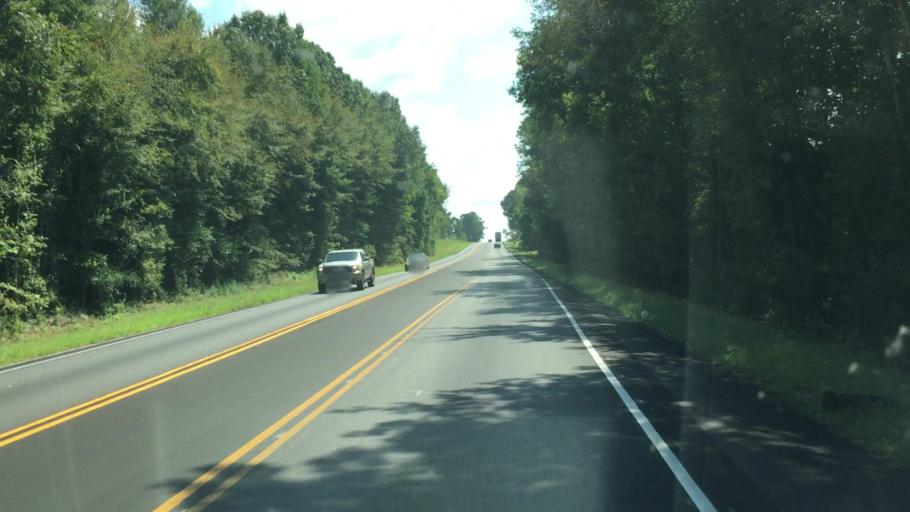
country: US
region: Georgia
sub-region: Morgan County
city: Madison
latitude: 33.6622
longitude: -83.4454
